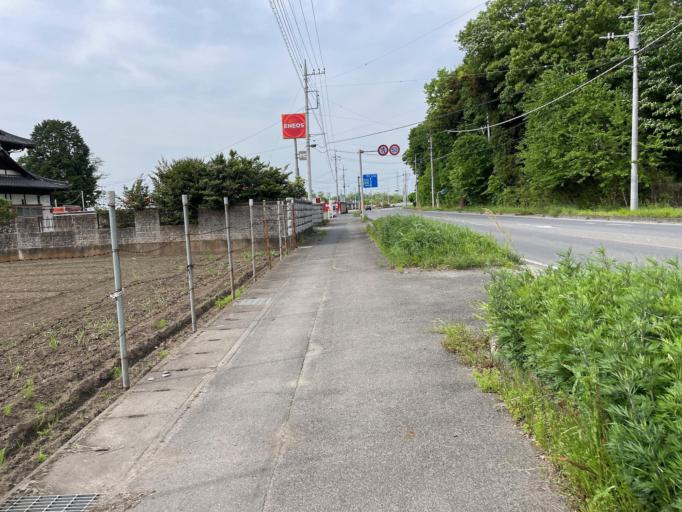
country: JP
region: Tochigi
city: Mibu
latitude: 36.4044
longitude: 139.8037
